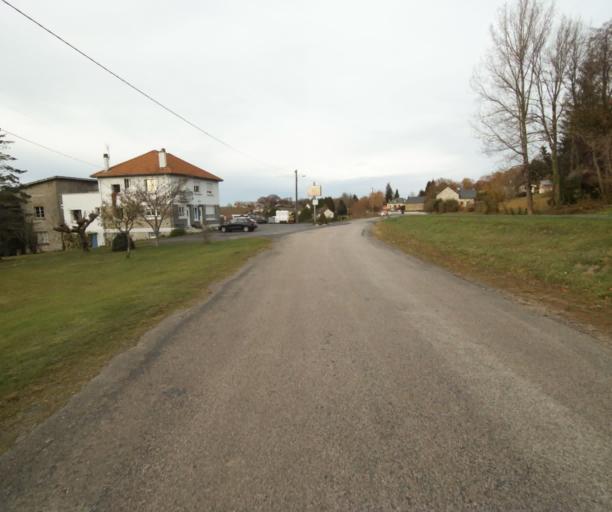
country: FR
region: Limousin
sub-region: Departement de la Correze
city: Sainte-Fortunade
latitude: 45.2206
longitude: 1.7672
